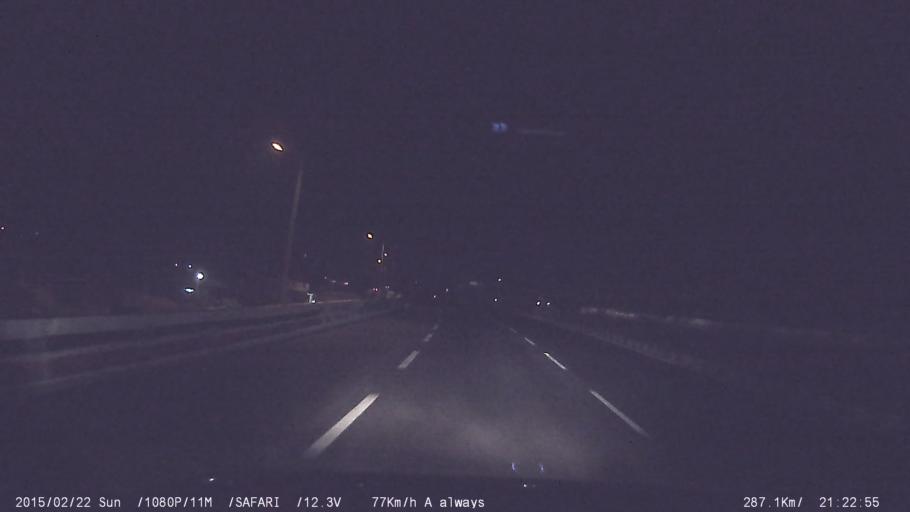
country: IN
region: Tamil Nadu
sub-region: Karur
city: Karur
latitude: 10.8753
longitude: 78.0056
